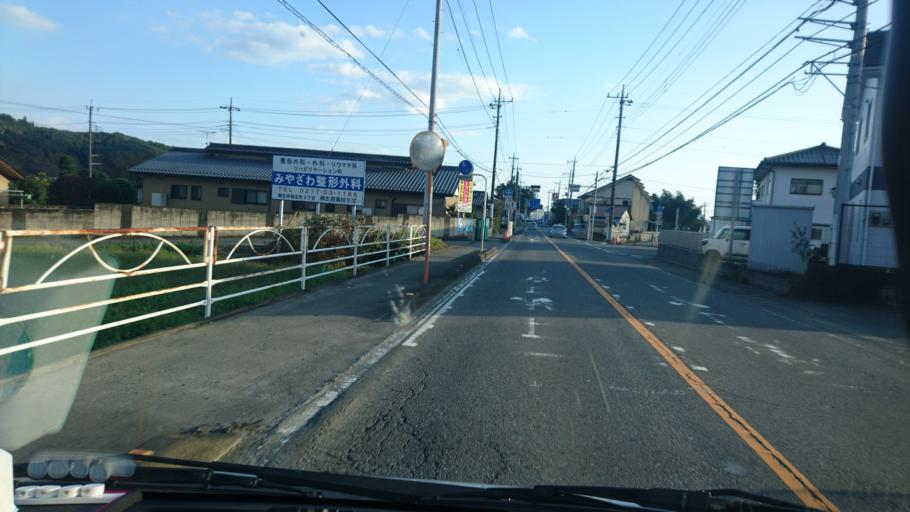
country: JP
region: Gunma
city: Omamacho-omama
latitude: 36.4484
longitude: 139.2749
